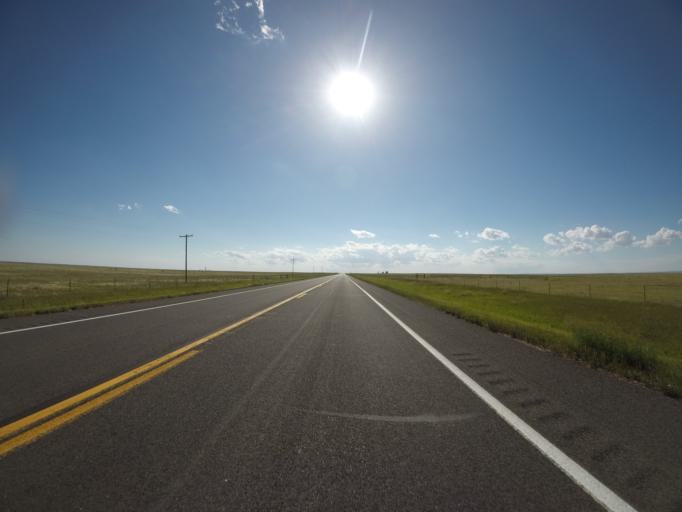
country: US
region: Colorado
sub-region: Morgan County
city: Brush
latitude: 40.6102
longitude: -103.6473
